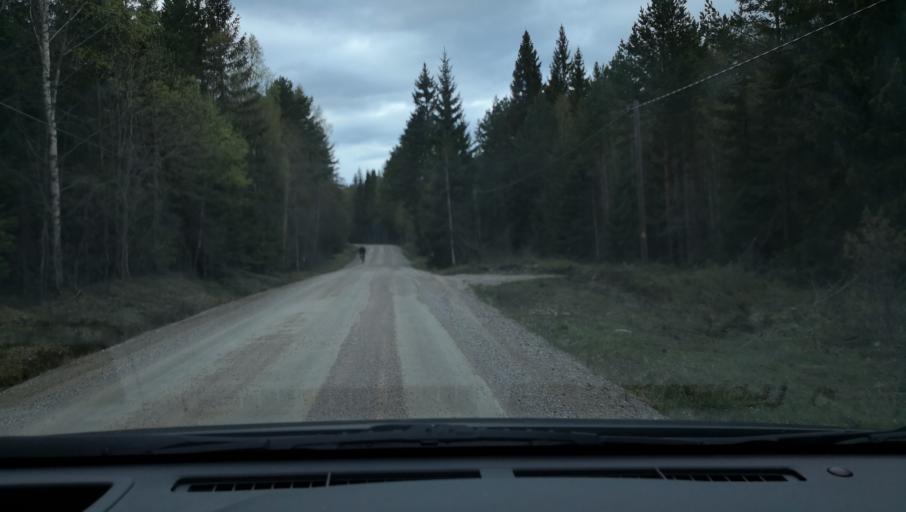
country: SE
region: Vaestmanland
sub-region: Norbergs Kommun
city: Norberg
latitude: 60.0907
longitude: 15.8658
